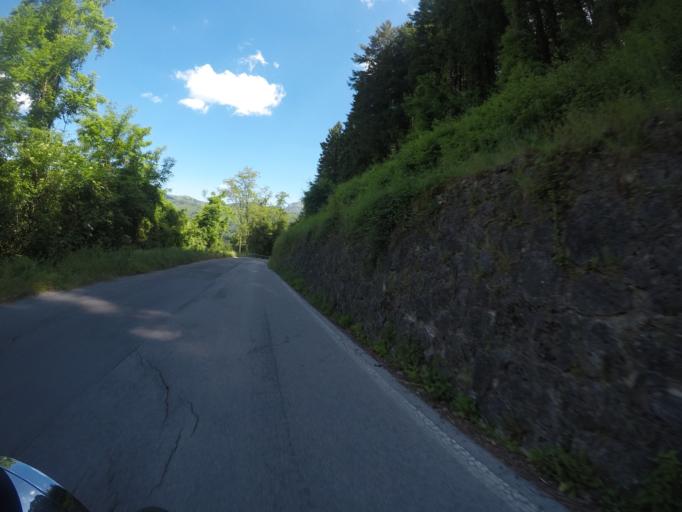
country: IT
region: Tuscany
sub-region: Provincia di Lucca
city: Camporgiano
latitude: 44.1424
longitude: 10.3501
